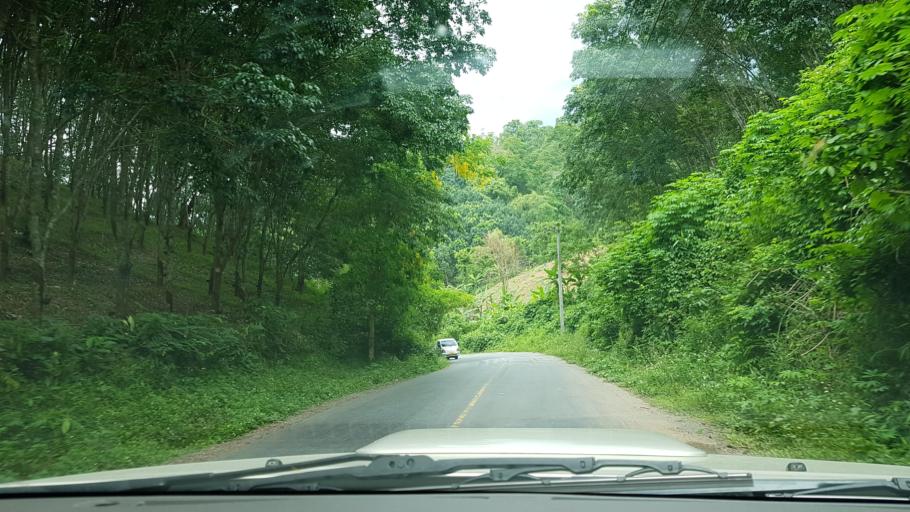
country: LA
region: Loungnamtha
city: Muang Nale
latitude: 20.3554
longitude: 101.6935
